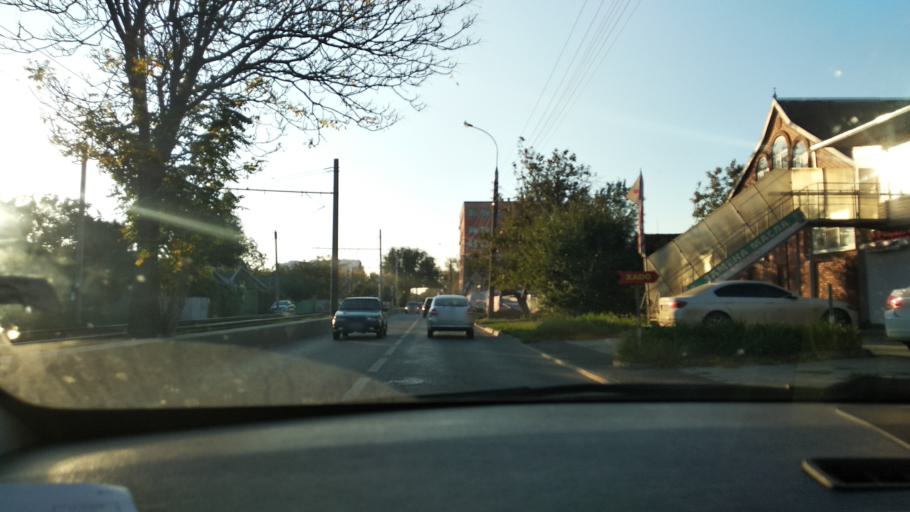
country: RU
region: Krasnodarskiy
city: Krasnodar
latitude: 45.0097
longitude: 39.0137
